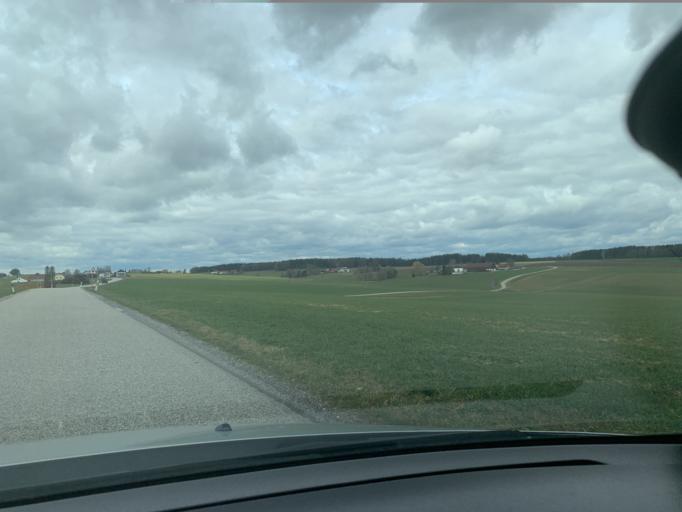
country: DE
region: Bavaria
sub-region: Lower Bavaria
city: Vilsbiburg
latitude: 48.4659
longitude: 12.3179
